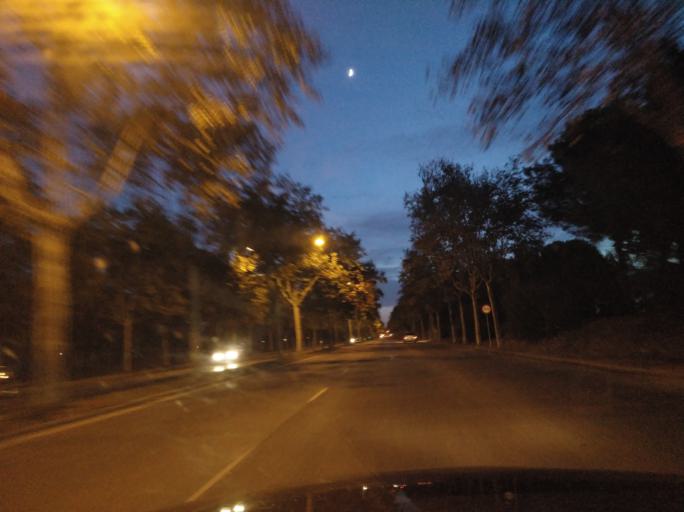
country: ES
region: Andalusia
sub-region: Provincia de Sevilla
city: Camas
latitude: 37.4032
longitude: -6.0106
